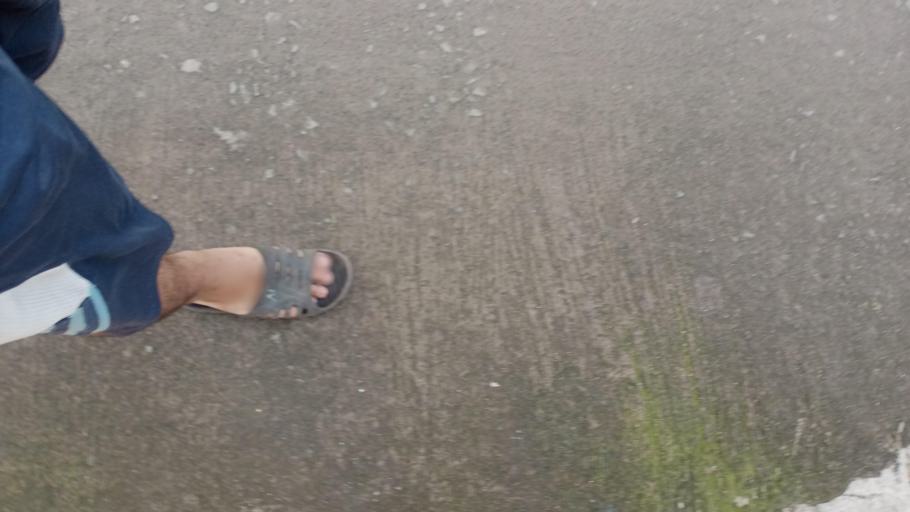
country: ID
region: West Java
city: Cikarang
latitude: -6.2641
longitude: 107.1158
